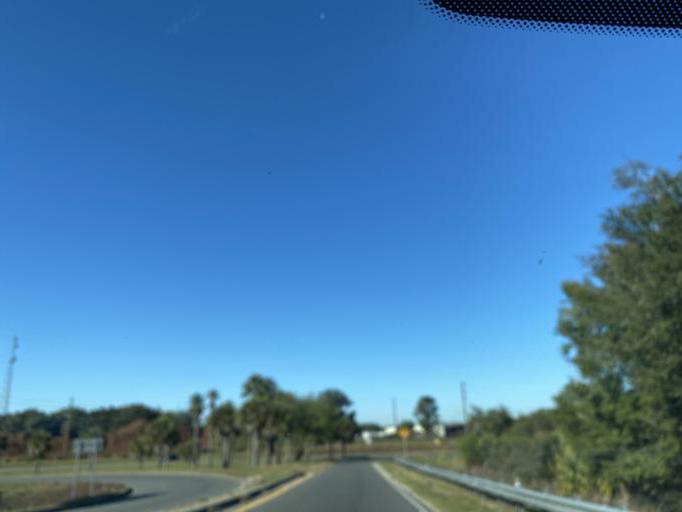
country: US
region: Florida
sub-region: Lake County
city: Howie In The Hills
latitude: 28.6427
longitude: -81.8046
